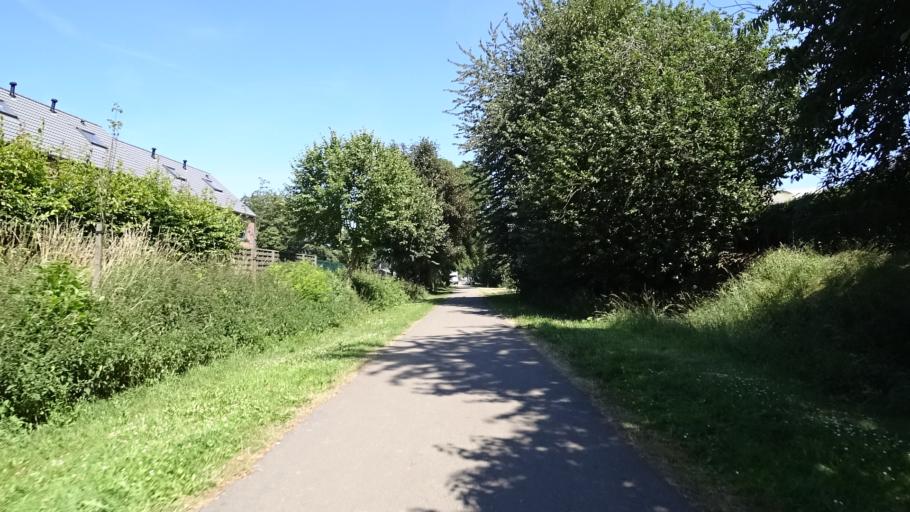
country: BE
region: Wallonia
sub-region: Province du Brabant Wallon
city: Perwez
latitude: 50.6228
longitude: 4.8029
